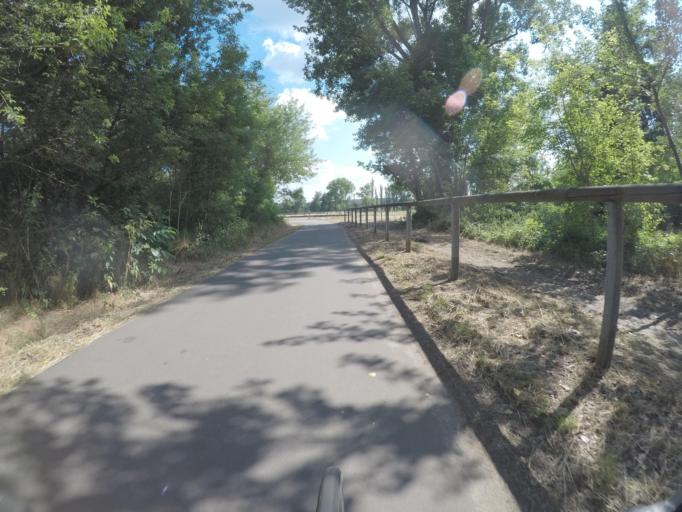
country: DE
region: Brandenburg
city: Ketzin
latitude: 52.4366
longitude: 12.8709
